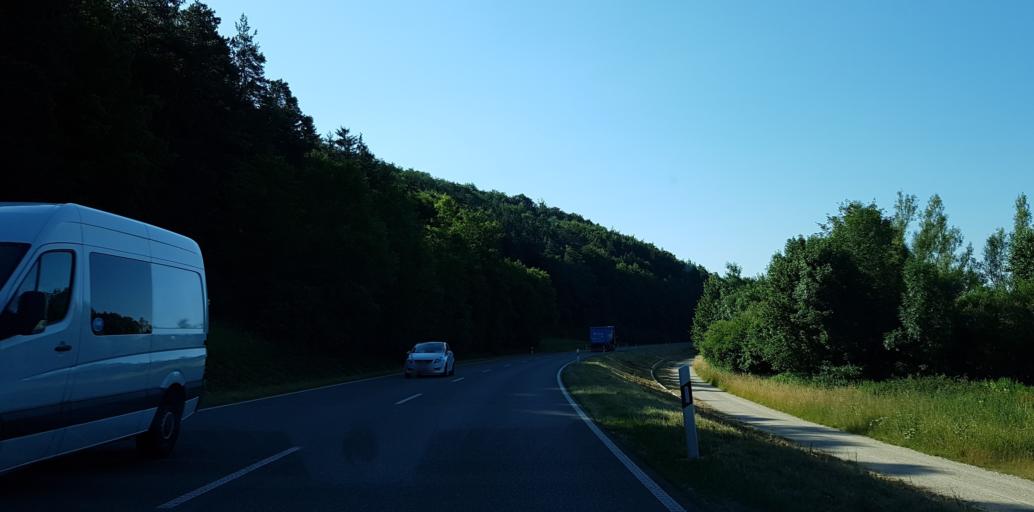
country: DE
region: Baden-Wuerttemberg
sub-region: Tuebingen Region
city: Allmendingen
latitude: 48.3465
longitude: 9.7175
